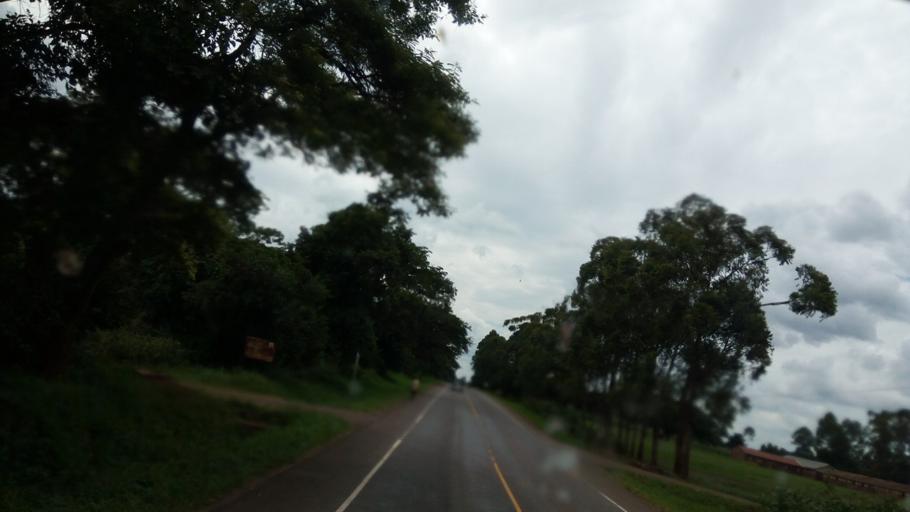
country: UG
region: Western Region
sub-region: Kiryandongo District
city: Kiryandongo
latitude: 2.0801
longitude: 32.1935
